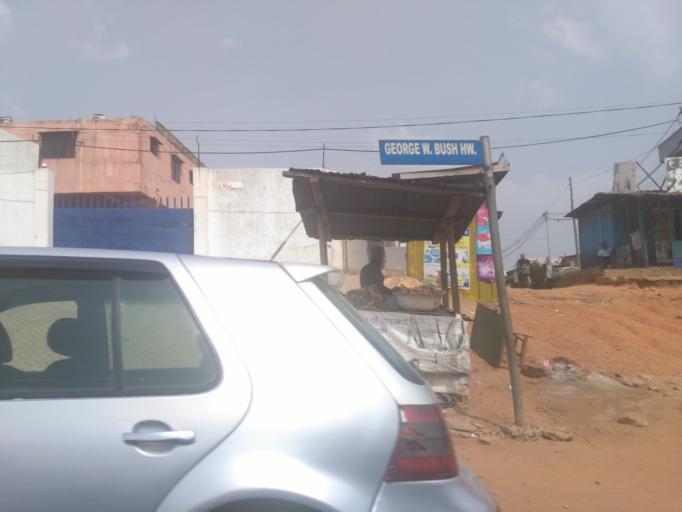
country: GH
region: Greater Accra
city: Dome
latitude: 5.6091
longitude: -0.2397
